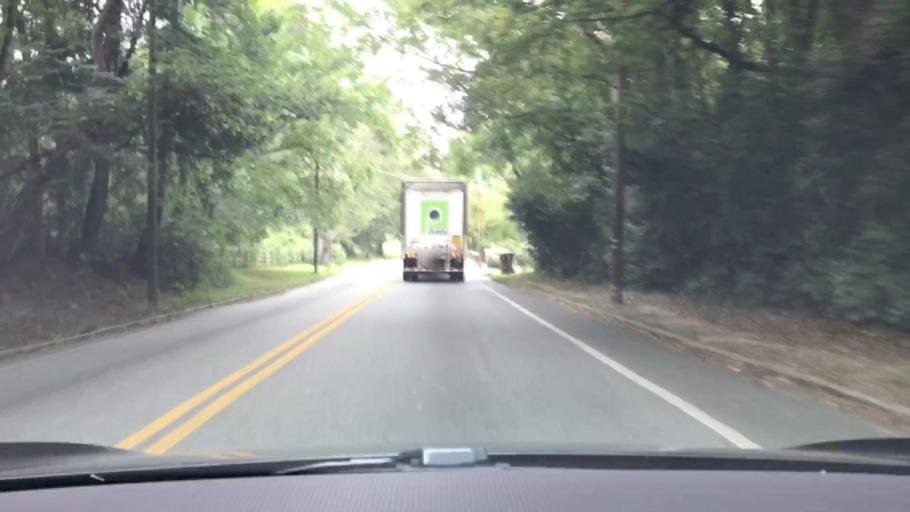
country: US
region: Georgia
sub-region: Greene County
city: Greensboro
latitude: 33.5776
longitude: -83.1880
